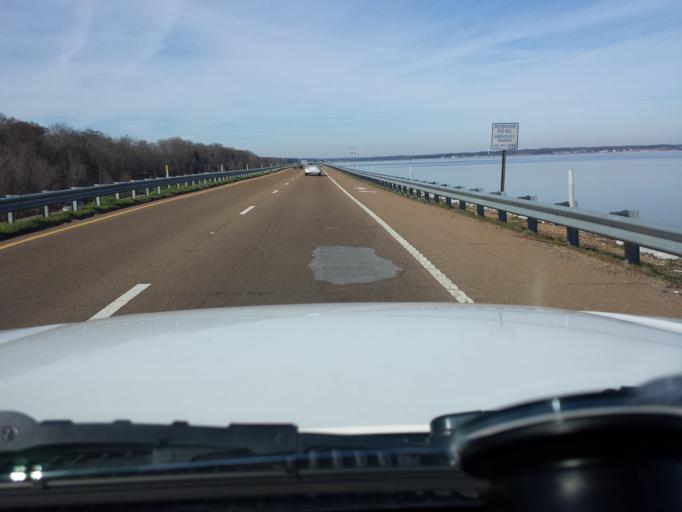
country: US
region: Mississippi
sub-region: Madison County
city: Ridgeland
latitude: 32.3885
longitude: -90.0506
